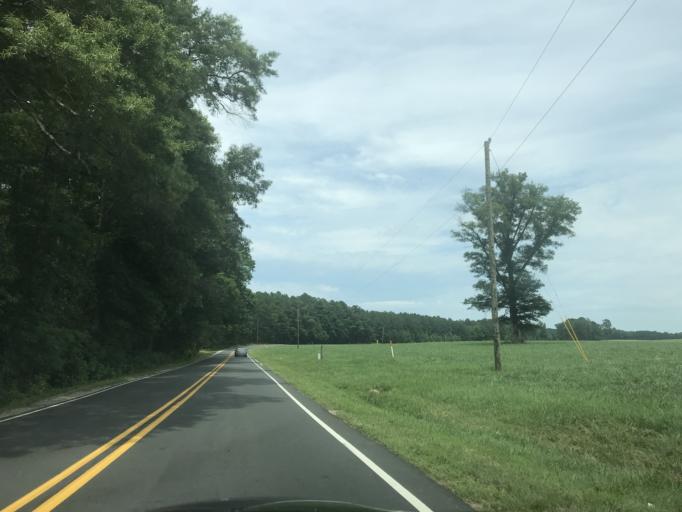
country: US
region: North Carolina
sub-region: Vance County
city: South Henderson
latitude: 36.2964
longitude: -78.4267
